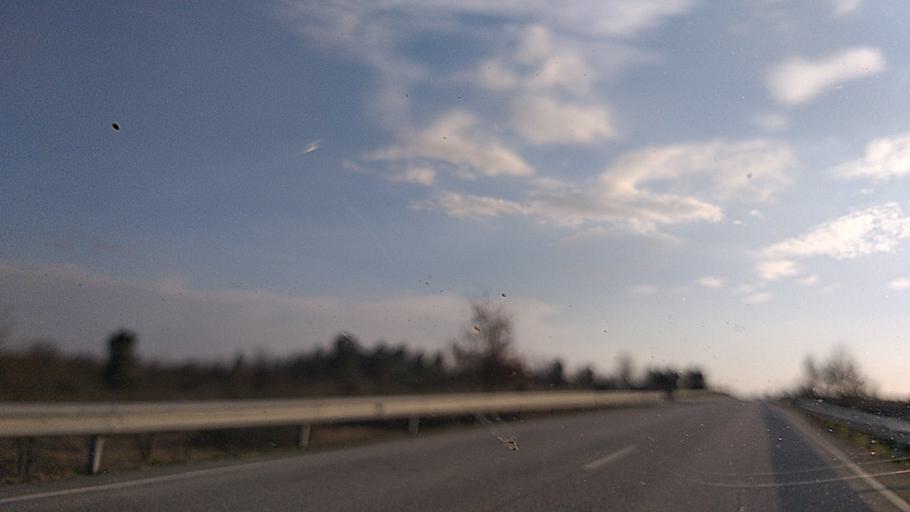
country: ES
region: Castille and Leon
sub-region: Provincia de Salamanca
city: Fuentes de Onoro
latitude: 40.6027
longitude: -6.9867
